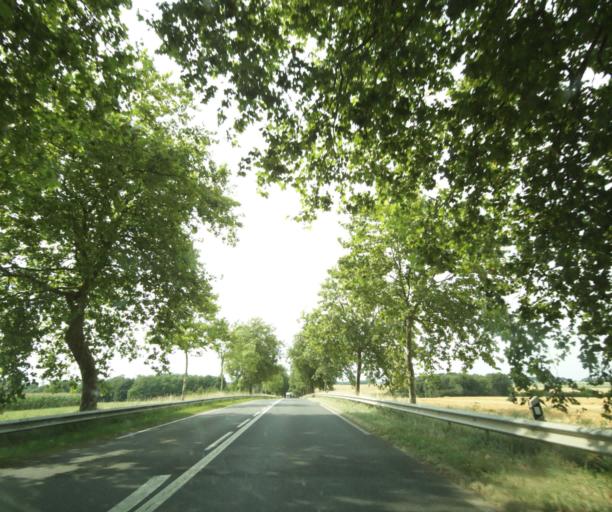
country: FR
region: Centre
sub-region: Departement d'Indre-et-Loire
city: Saint-Paterne-Racan
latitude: 47.5996
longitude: 0.5228
